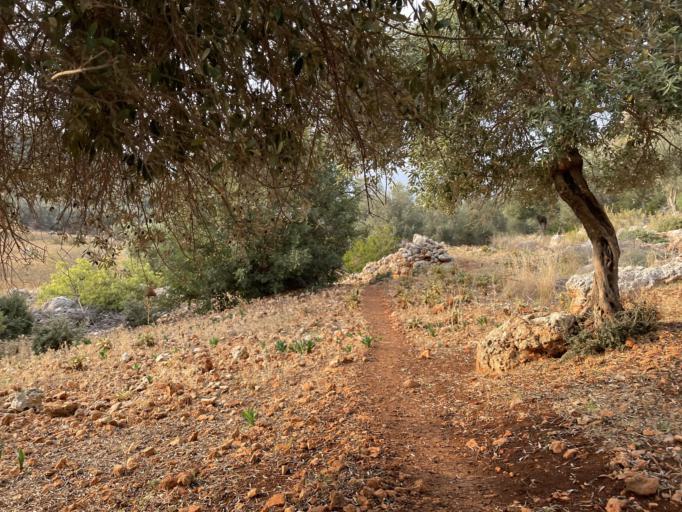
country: TR
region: Antalya
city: Kas
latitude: 36.1685
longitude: 29.6531
